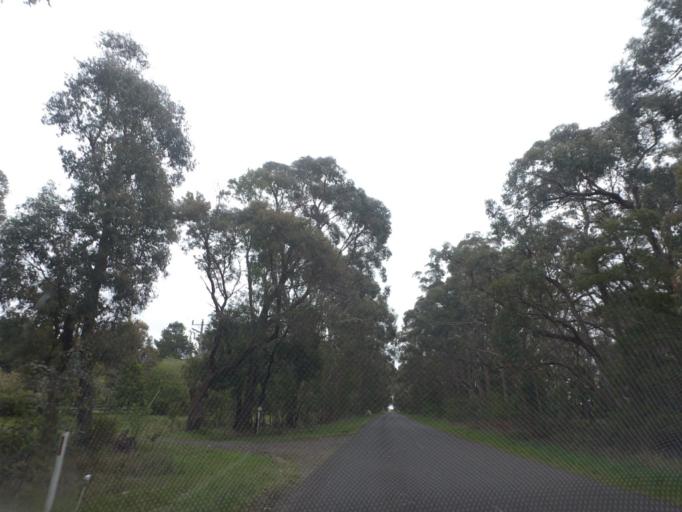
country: AU
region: Victoria
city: Brown Hill
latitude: -37.5896
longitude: 144.1188
